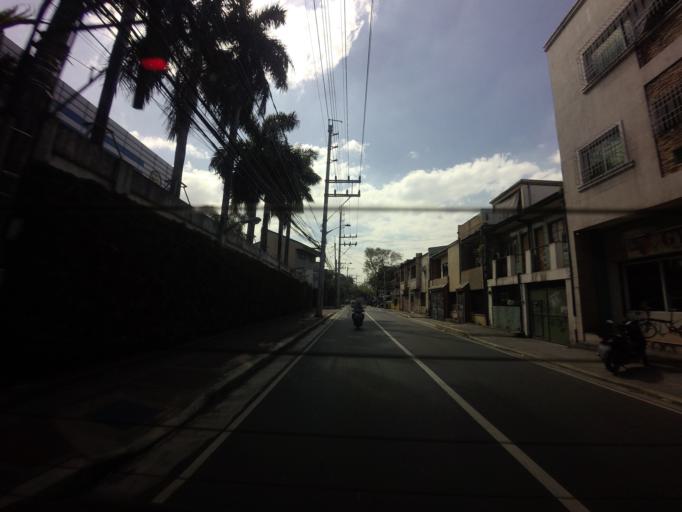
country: PH
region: Metro Manila
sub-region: San Juan
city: San Juan
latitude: 14.6112
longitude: 121.0143
